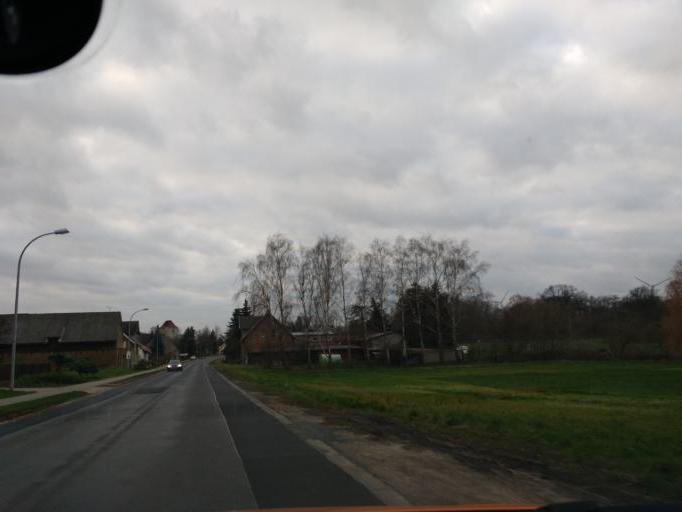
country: DE
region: Brandenburg
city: Wriezen
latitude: 52.6906
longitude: 14.1022
